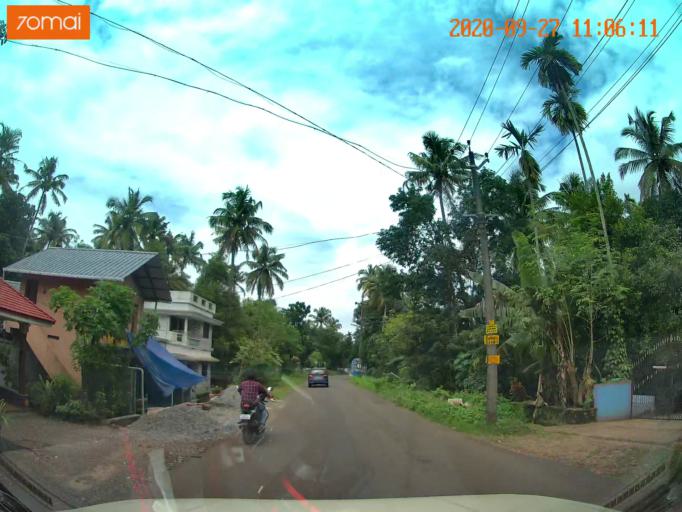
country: IN
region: Kerala
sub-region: Thrissur District
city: Irinjalakuda
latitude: 10.4247
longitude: 76.2439
